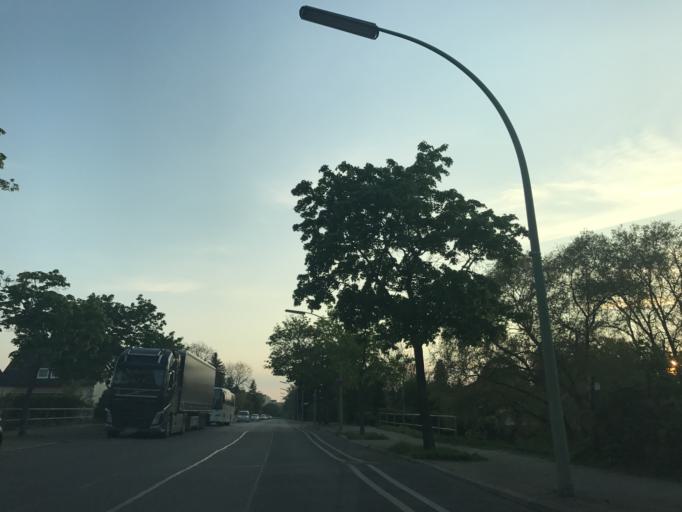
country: DE
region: Berlin
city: Wilhelmstadt
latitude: 52.5263
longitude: 13.1670
